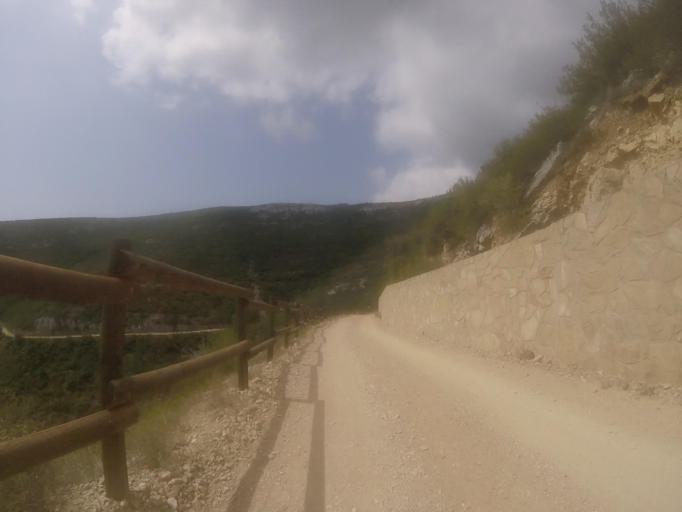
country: ES
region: Valencia
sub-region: Provincia de Castello
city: Peniscola
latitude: 40.3465
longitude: 0.3565
